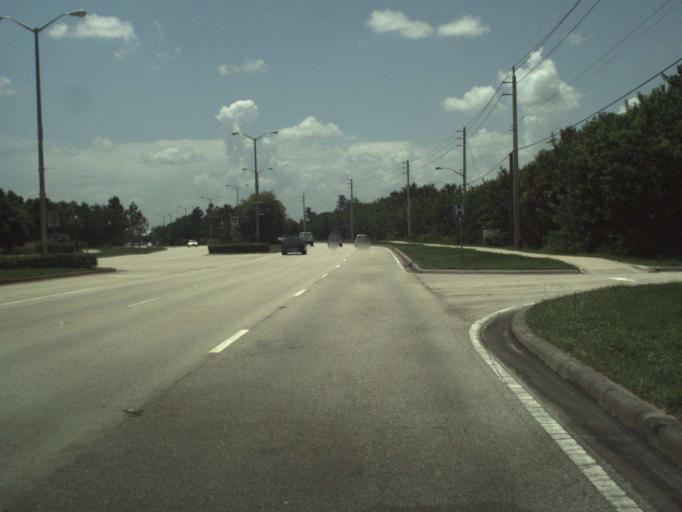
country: US
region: Florida
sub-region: Saint Lucie County
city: Port Saint Lucie
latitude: 27.2643
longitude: -80.3937
